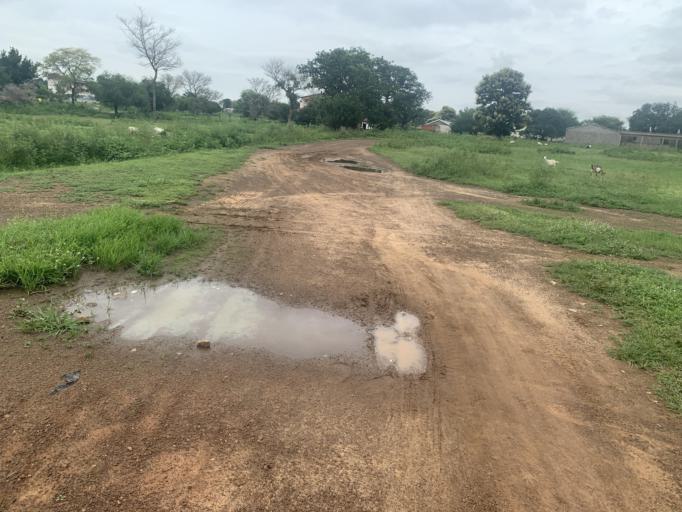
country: GH
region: Upper East
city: Navrongo
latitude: 10.8656
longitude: -1.0815
